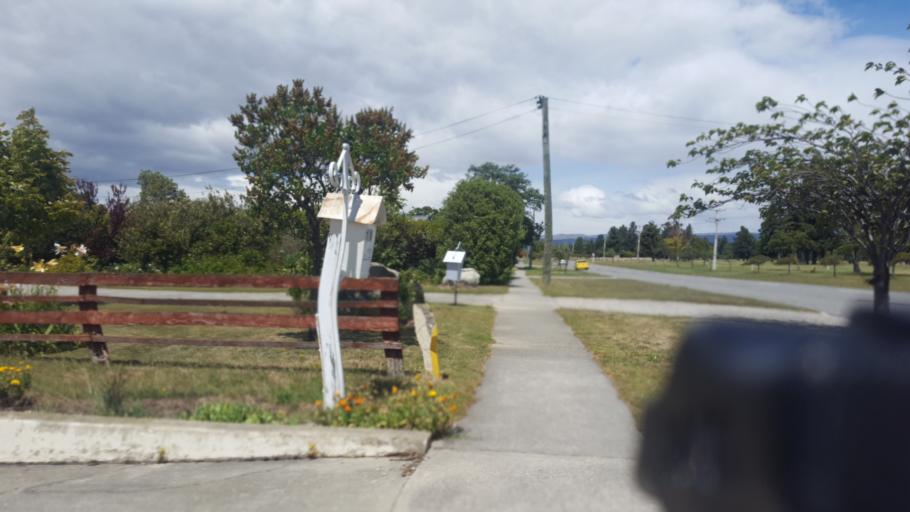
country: NZ
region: Otago
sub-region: Queenstown-Lakes District
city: Wanaka
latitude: -45.1934
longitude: 169.3253
